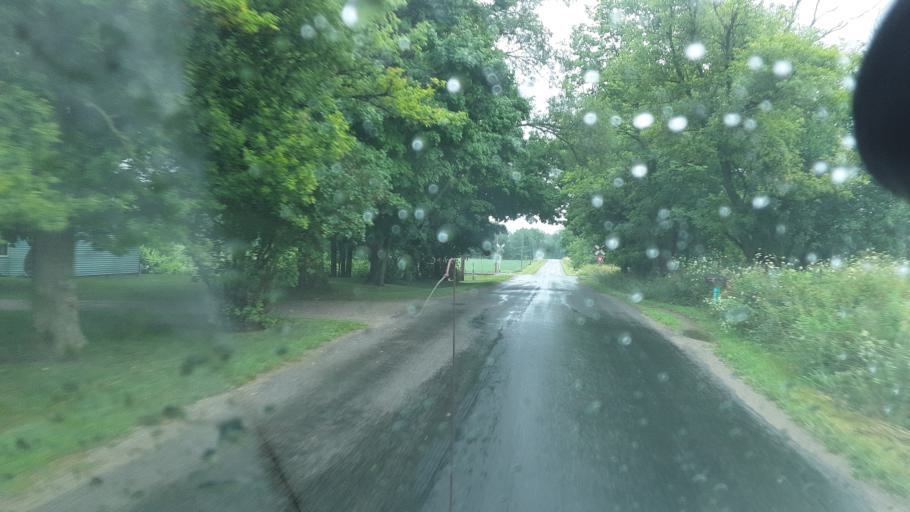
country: US
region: Indiana
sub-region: Steuben County
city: Hamilton
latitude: 41.5415
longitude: -84.8548
